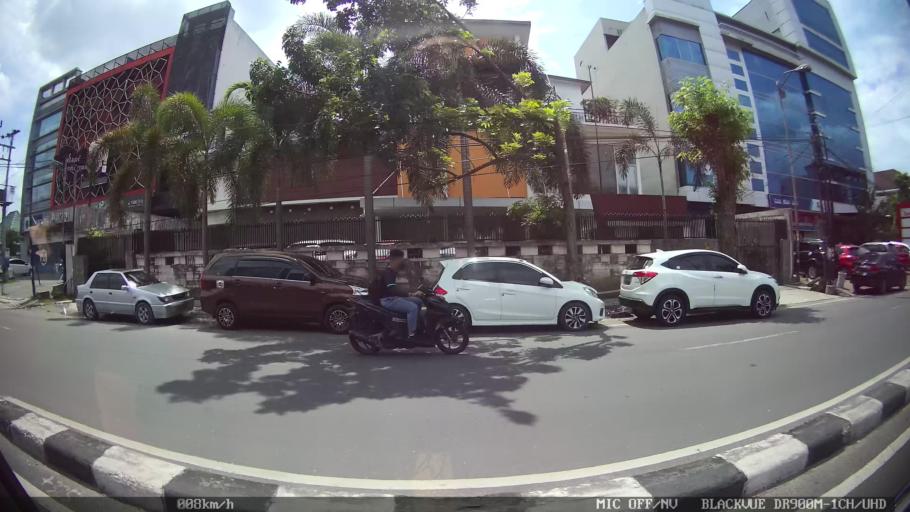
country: ID
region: North Sumatra
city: Medan
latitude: 3.5739
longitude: 98.6609
